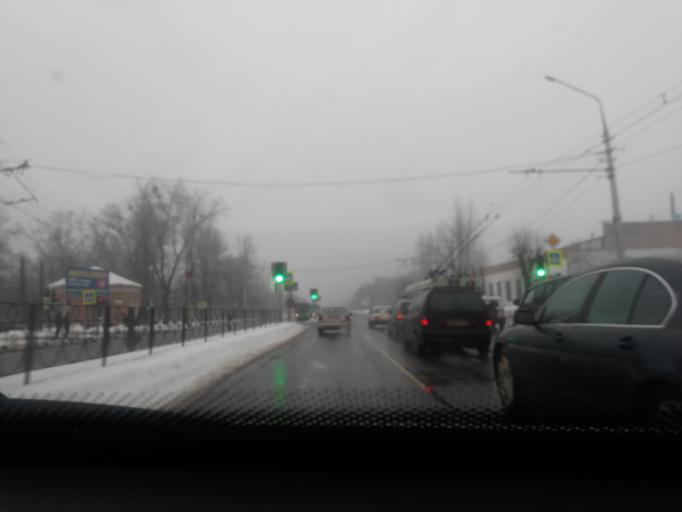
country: BY
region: Mogilev
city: Babruysk
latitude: 53.1651
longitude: 29.2092
